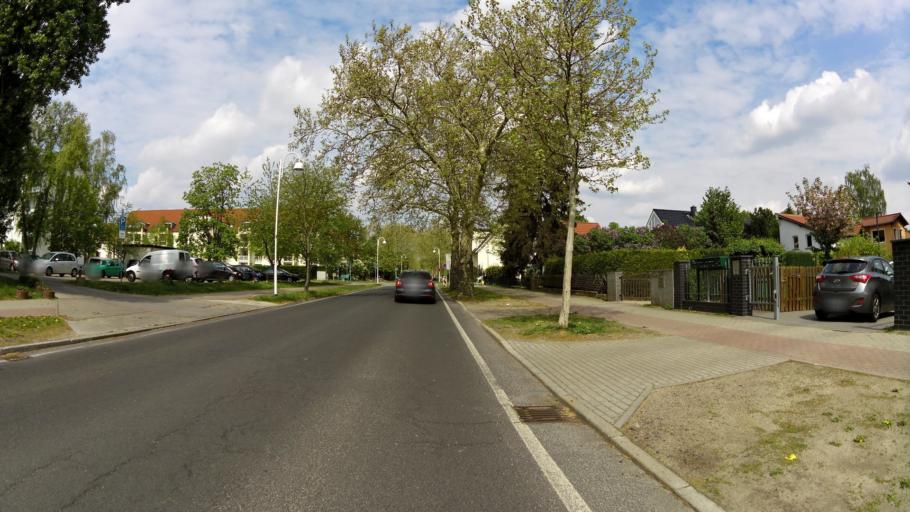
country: DE
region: Berlin
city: Lichtenrade
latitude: 52.3646
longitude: 13.4123
